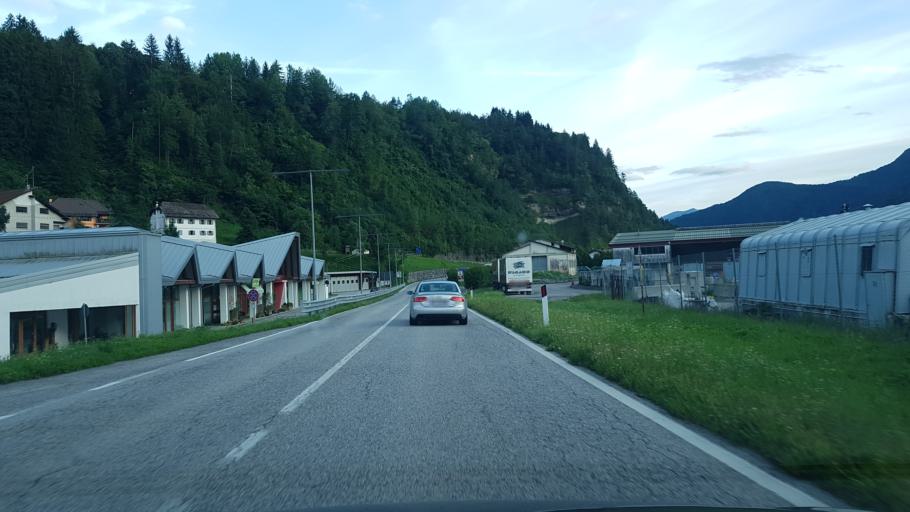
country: IT
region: Friuli Venezia Giulia
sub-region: Provincia di Udine
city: Comeglians
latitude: 46.5133
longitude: 12.8662
